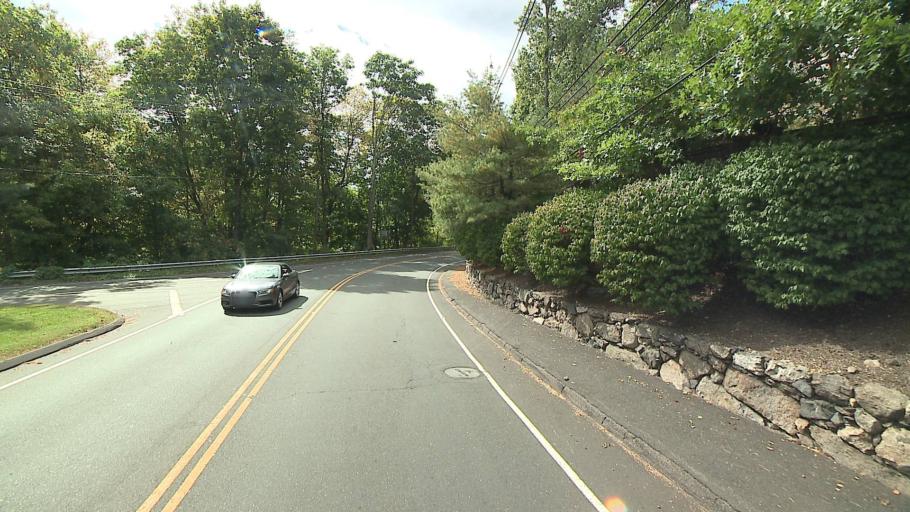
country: US
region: Connecticut
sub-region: Fairfield County
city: New Canaan
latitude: 41.1484
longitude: -73.4830
